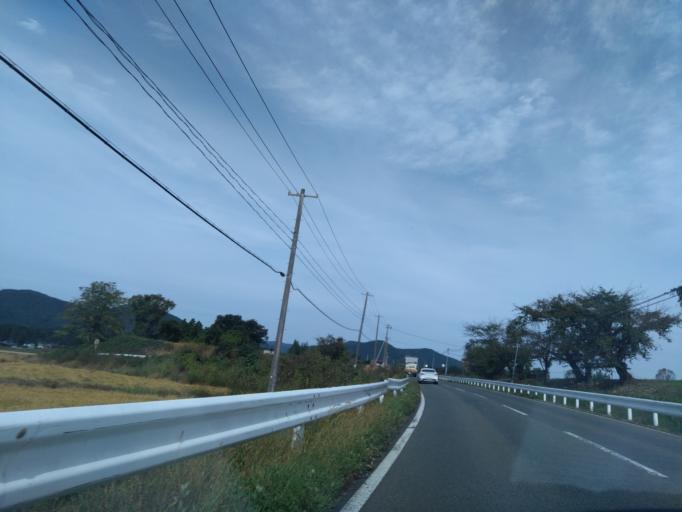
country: JP
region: Iwate
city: Hanamaki
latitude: 39.4300
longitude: 141.0839
